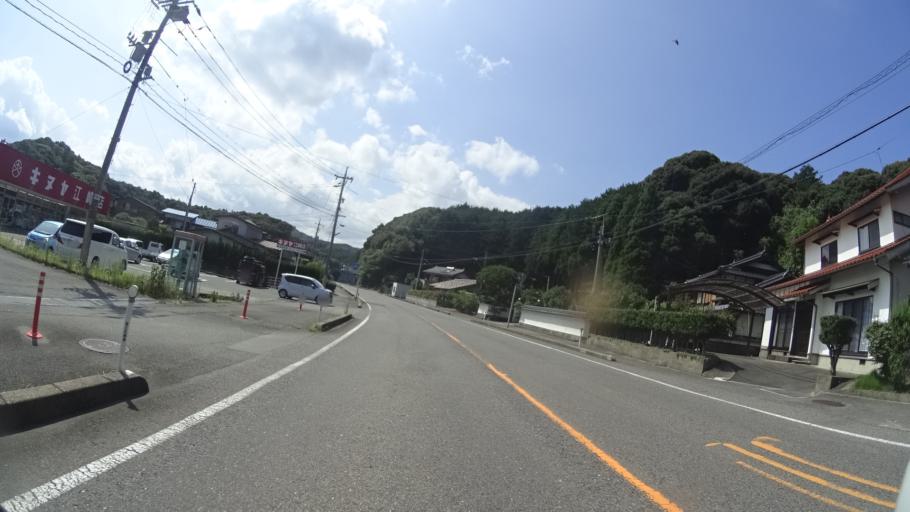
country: JP
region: Shimane
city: Masuda
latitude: 34.6452
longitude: 131.6615
